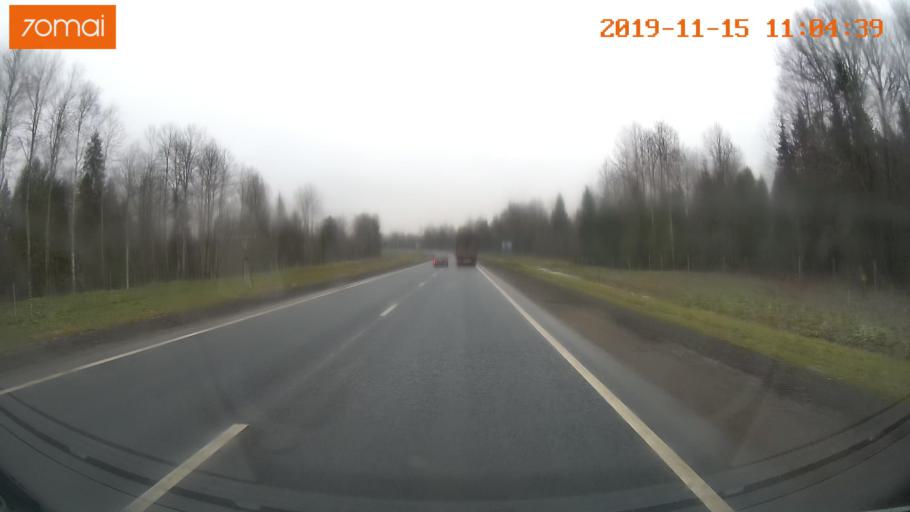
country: RU
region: Vologda
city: Chebsara
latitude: 59.1193
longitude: 38.9884
